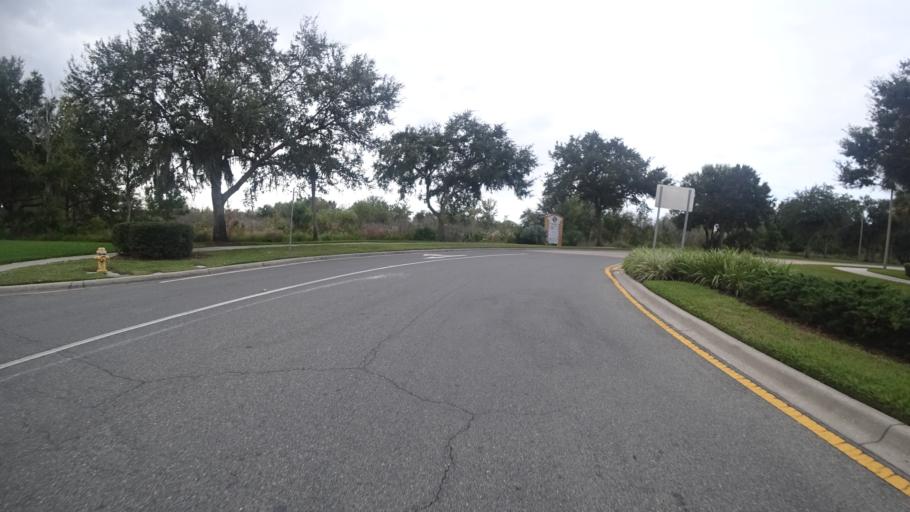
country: US
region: Florida
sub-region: Sarasota County
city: The Meadows
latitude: 27.3877
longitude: -82.4421
